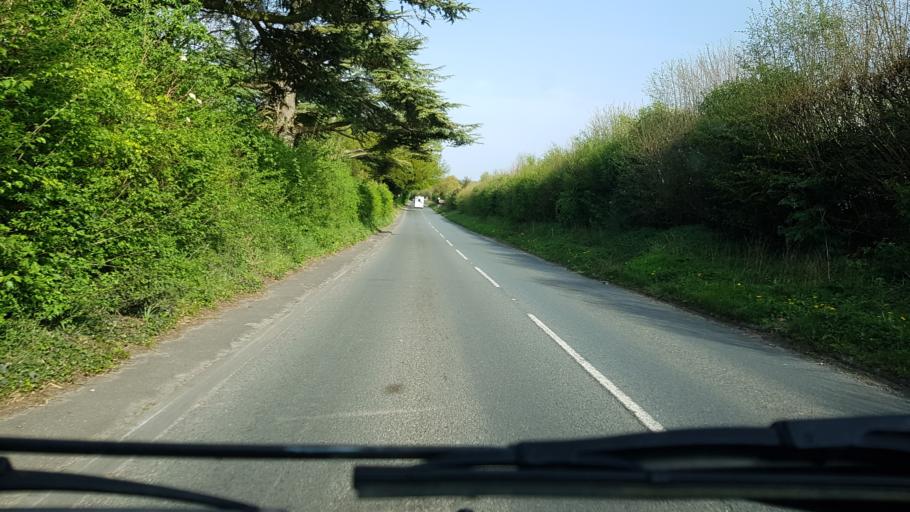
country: GB
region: England
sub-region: Hampshire
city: Basingstoke
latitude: 51.2617
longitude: -1.1506
